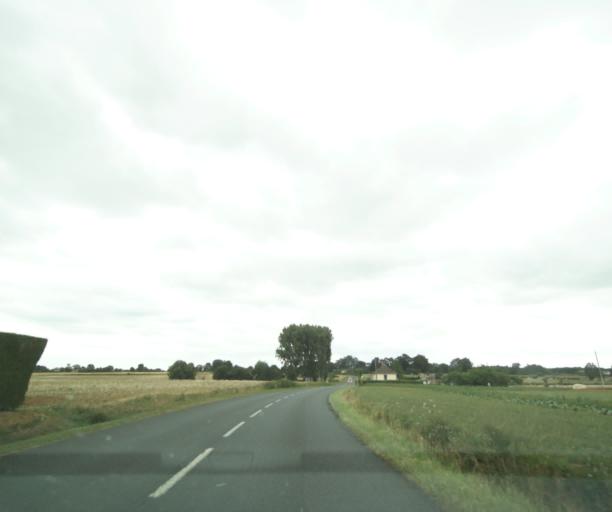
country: FR
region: Pays de la Loire
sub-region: Departement de la Sarthe
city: Precigne
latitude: 47.7795
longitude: -0.3178
